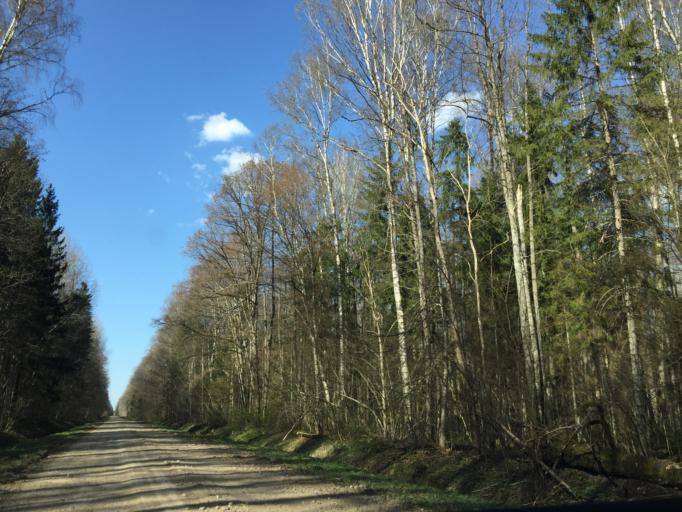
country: LV
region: Lielvarde
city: Lielvarde
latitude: 56.8560
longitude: 24.8022
